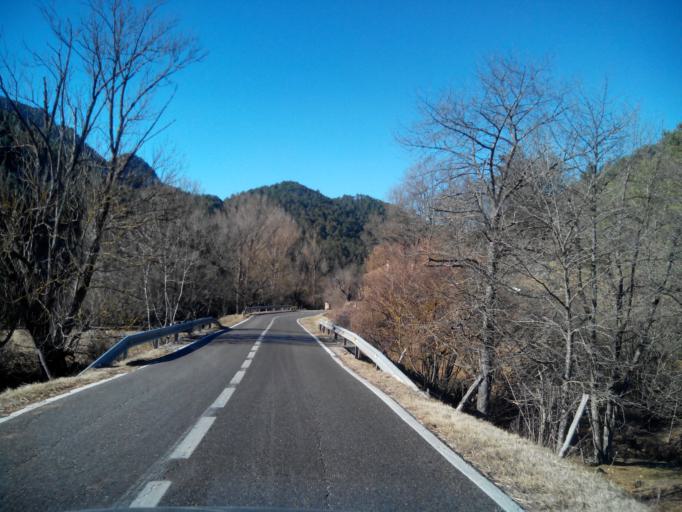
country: ES
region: Catalonia
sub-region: Provincia de Barcelona
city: Capolat
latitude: 42.1041
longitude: 1.7336
